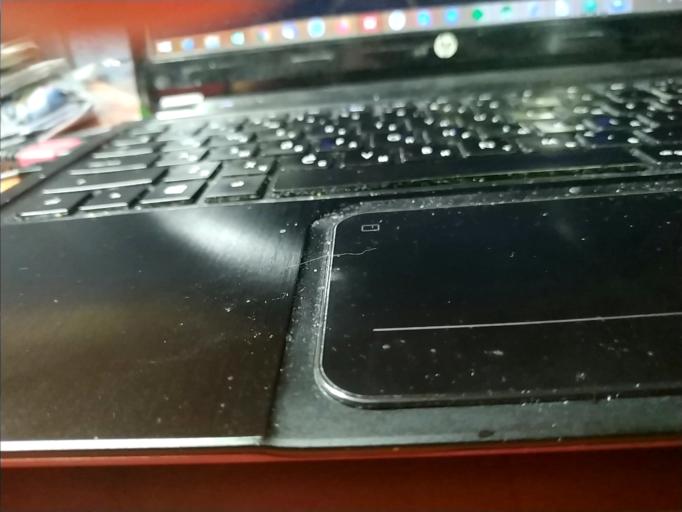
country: RU
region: Tverskaya
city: Ves'yegonsk
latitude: 58.7046
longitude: 37.5439
